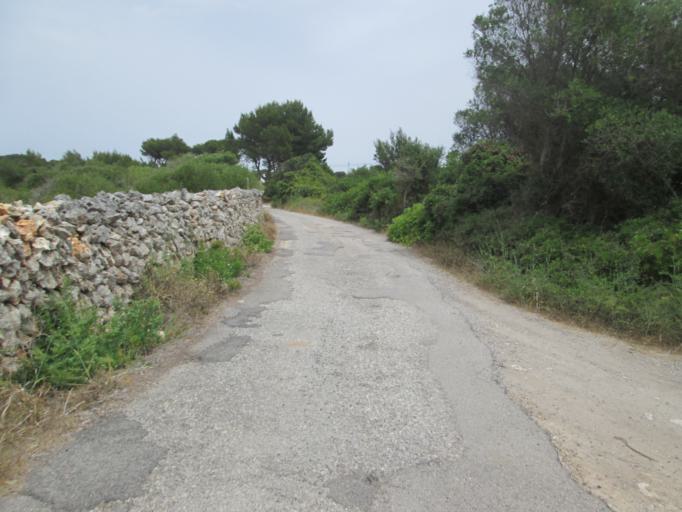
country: ES
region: Balearic Islands
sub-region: Illes Balears
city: Es Migjorn Gran
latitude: 39.9328
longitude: 4.0451
